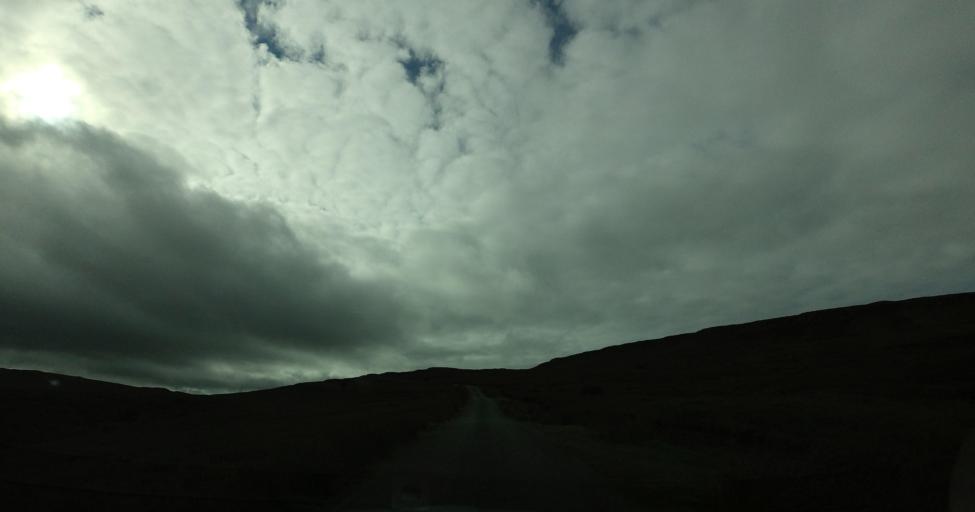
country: GB
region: Scotland
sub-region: Highland
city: Isle of Skye
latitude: 57.4167
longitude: -6.2574
